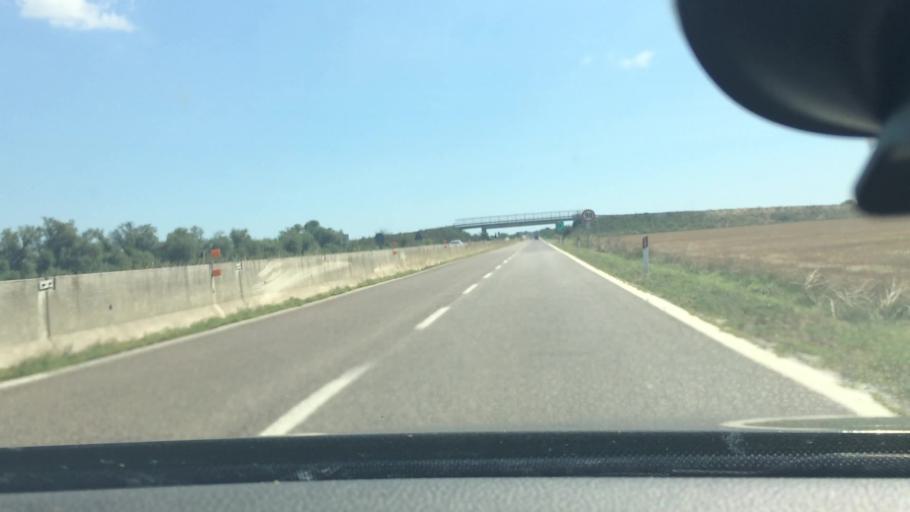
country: IT
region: Emilia-Romagna
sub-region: Provincia di Ferrara
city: Ostellato
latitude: 44.7544
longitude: 11.9800
